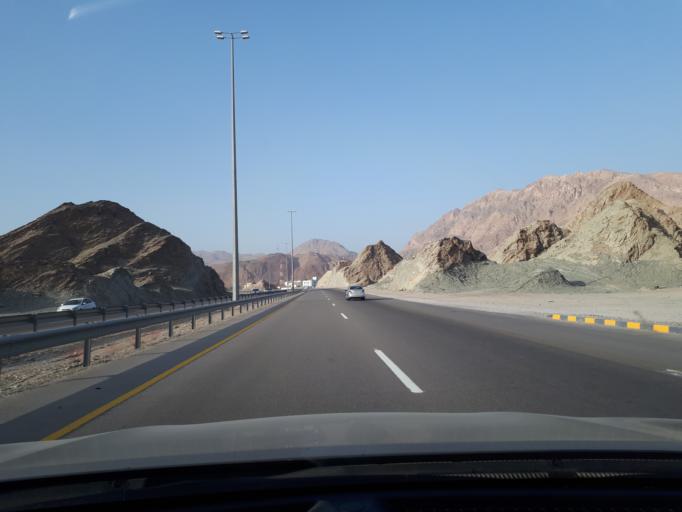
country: OM
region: Muhafazat Masqat
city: Bawshar
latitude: 23.4341
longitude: 58.5085
